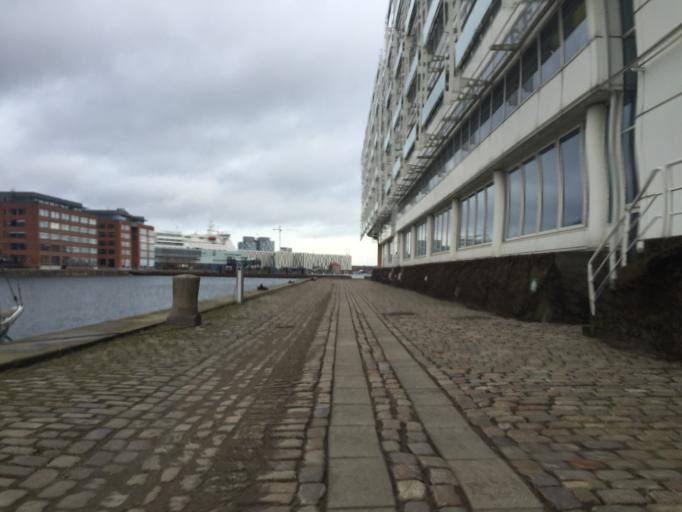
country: DK
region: Capital Region
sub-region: Kobenhavn
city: Christianshavn
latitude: 55.6980
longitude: 12.5971
